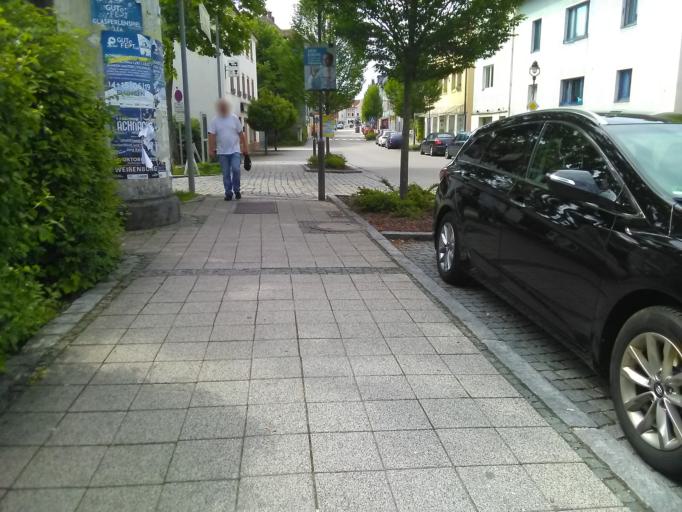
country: DE
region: Bavaria
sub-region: Regierungsbezirk Mittelfranken
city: Treuchtlingen
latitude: 48.9575
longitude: 10.9088
